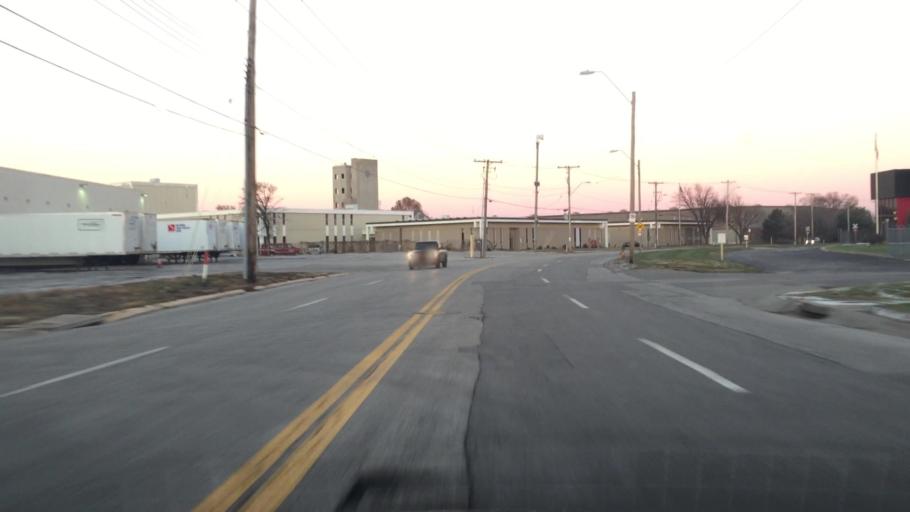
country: US
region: Missouri
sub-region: Clay County
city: North Kansas City
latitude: 39.1391
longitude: -94.5220
